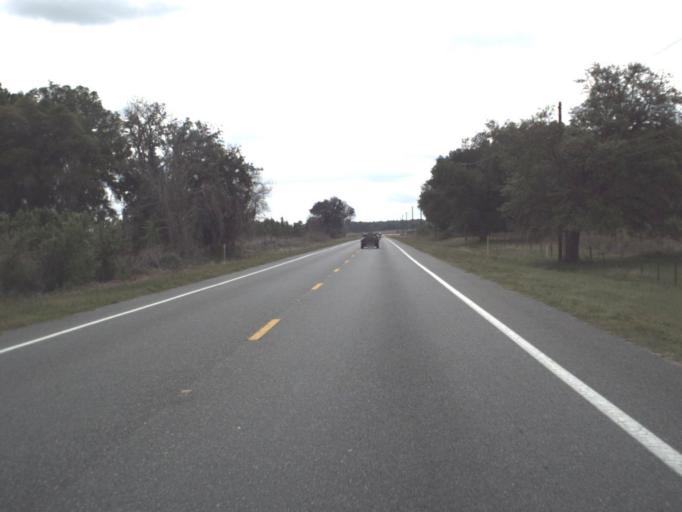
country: US
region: Florida
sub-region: Marion County
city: Ocala
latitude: 29.2593
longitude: -82.0837
